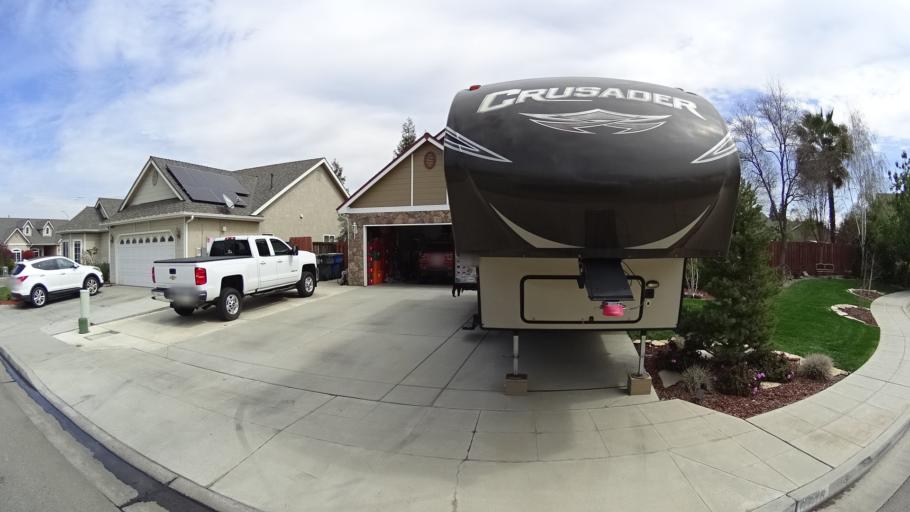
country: US
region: California
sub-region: Fresno County
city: Biola
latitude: 36.8358
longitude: -119.8920
